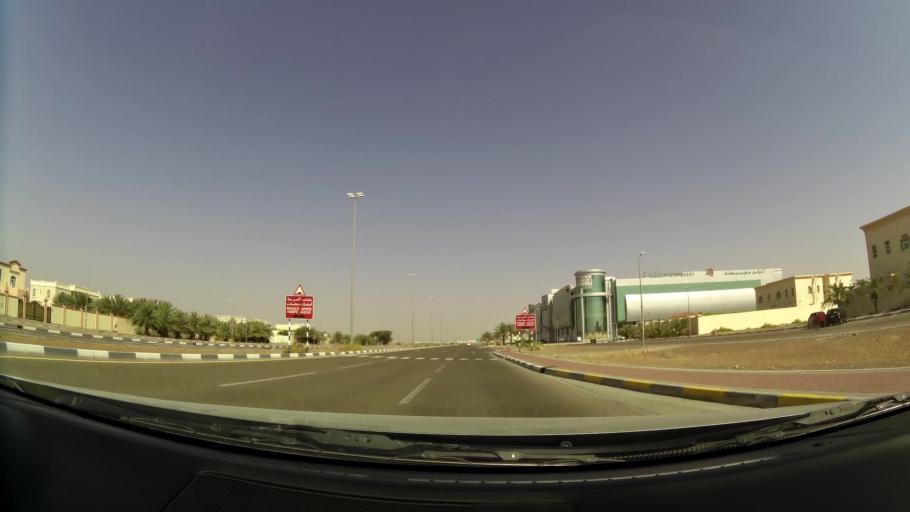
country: OM
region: Al Buraimi
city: Al Buraymi
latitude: 24.3427
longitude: 55.7945
